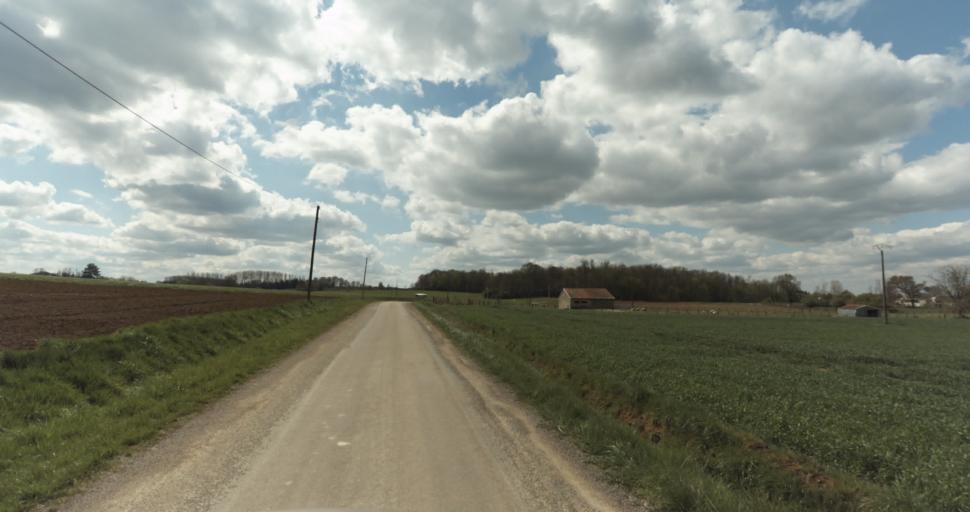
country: FR
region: Bourgogne
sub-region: Departement de la Cote-d'Or
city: Auxonne
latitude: 47.1887
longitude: 5.4202
